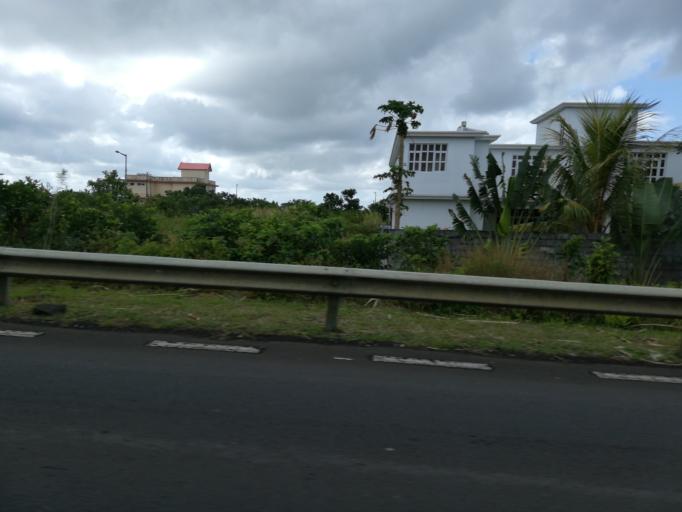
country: MU
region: Grand Port
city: New Grove
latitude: -20.4145
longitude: 57.6035
